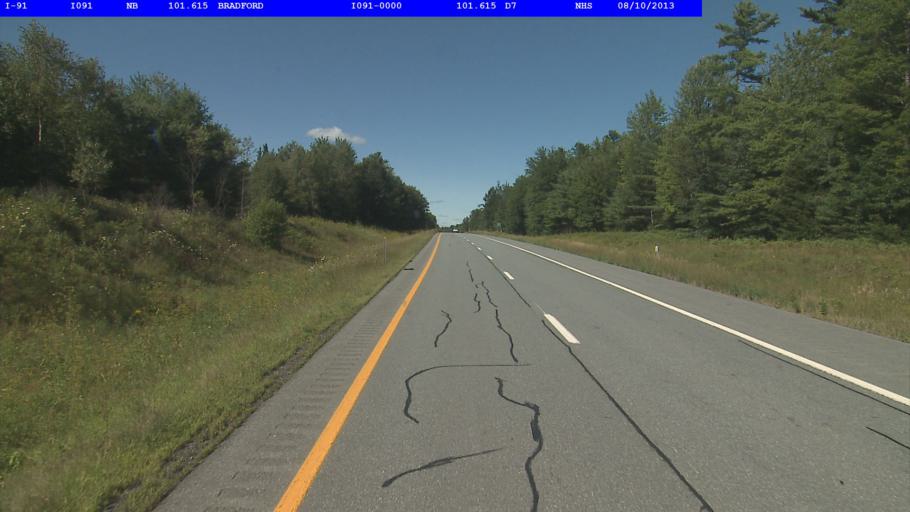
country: US
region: New Hampshire
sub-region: Grafton County
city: Haverhill
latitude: 44.0370
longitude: -72.1097
